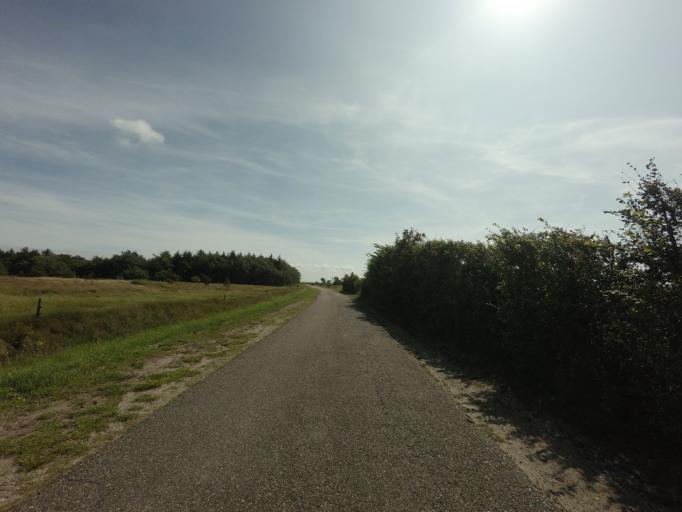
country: NL
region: Friesland
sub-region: Gemeente Ameland
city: Hollum
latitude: 53.4439
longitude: 5.6625
